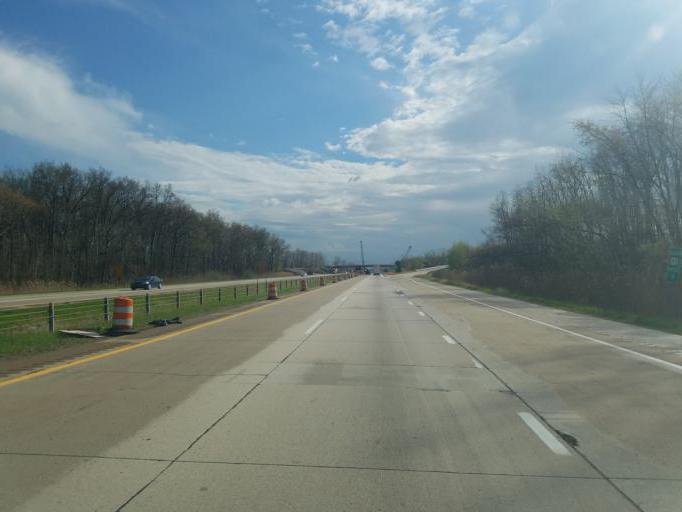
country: US
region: Michigan
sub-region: Monroe County
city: Petersburg
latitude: 41.8499
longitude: -83.6640
